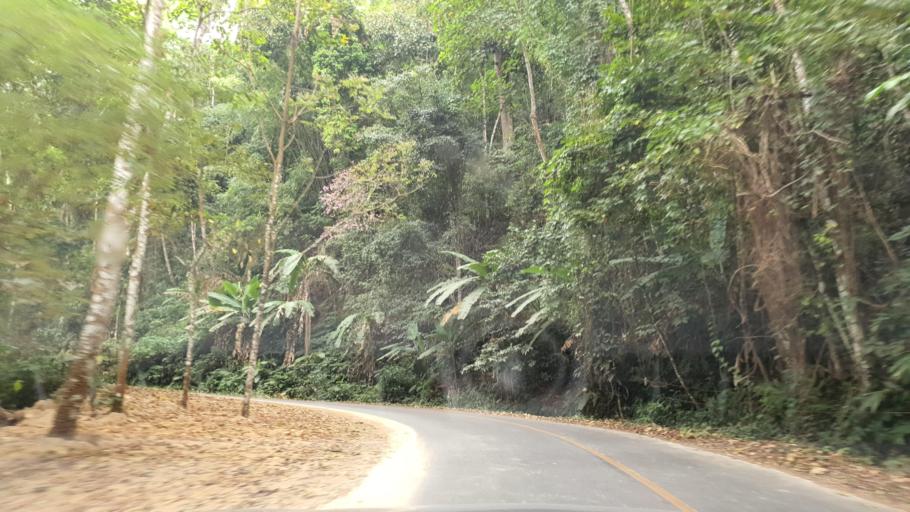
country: TH
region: Chiang Mai
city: Mae On
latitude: 18.9407
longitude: 99.3646
